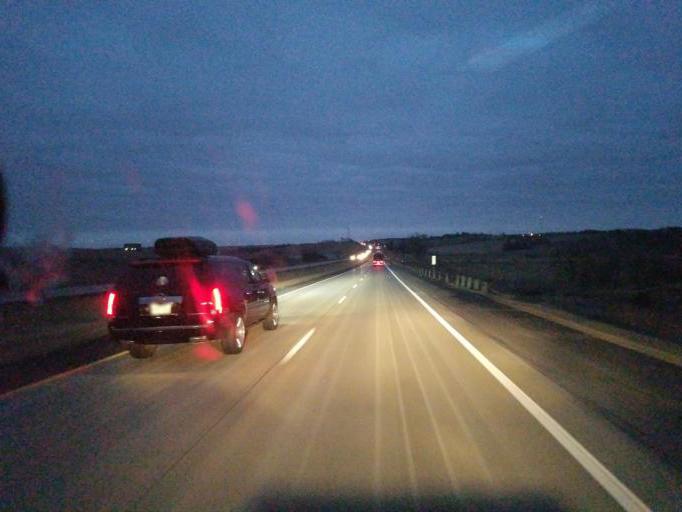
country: US
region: Iowa
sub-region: Cass County
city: Atlantic
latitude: 41.4966
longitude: -94.8034
